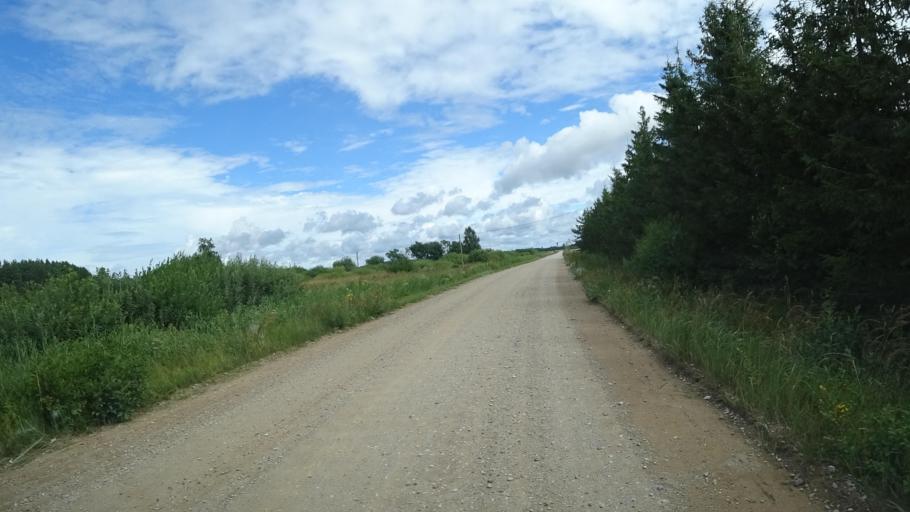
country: LV
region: Liepaja
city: Vec-Liepaja
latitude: 56.6491
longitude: 21.0458
